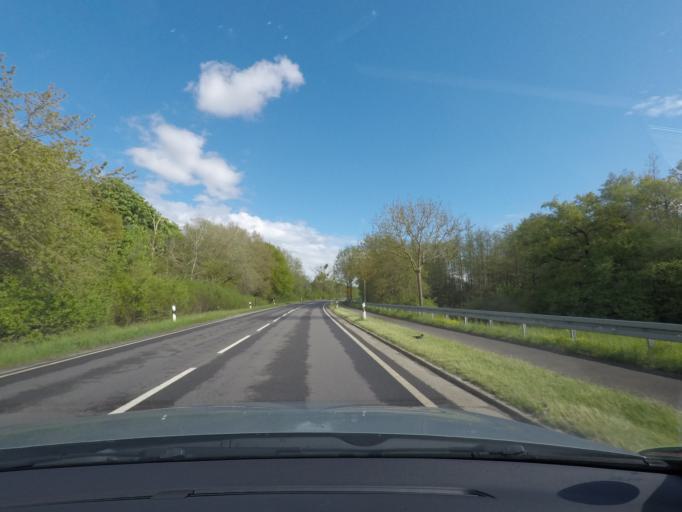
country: DE
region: Lower Saxony
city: Mariental
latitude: 52.2915
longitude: 10.9862
